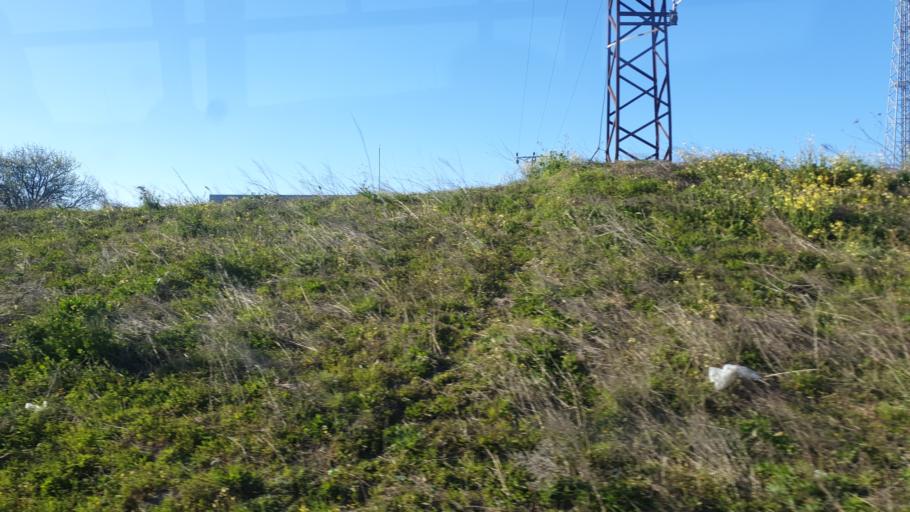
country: TR
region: Tekirdag
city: Velimese
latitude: 41.2573
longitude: 27.9058
